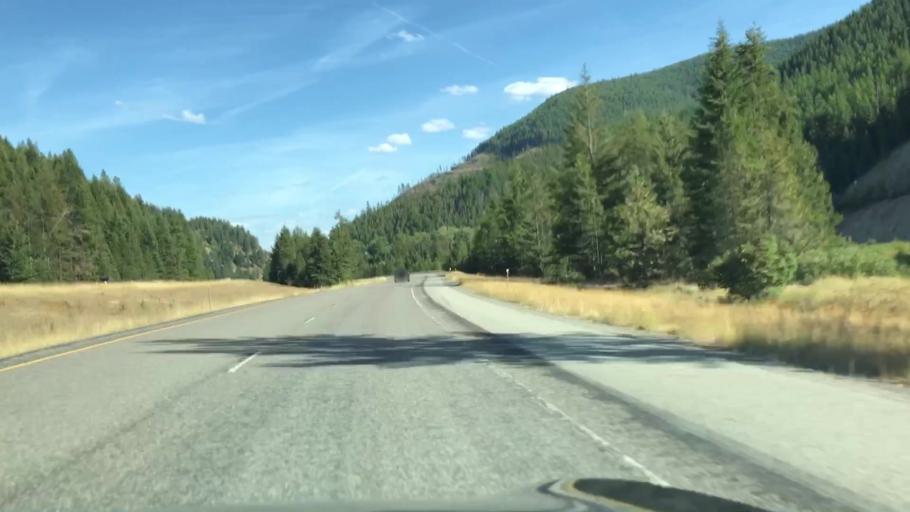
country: US
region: Montana
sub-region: Sanders County
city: Thompson Falls
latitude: 47.4067
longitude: -115.4915
